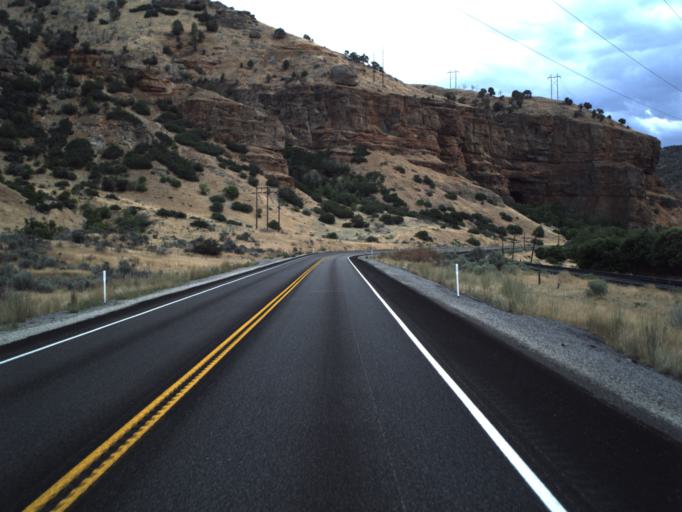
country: US
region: Utah
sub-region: Utah County
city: Mapleton
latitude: 39.9969
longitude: -111.4075
